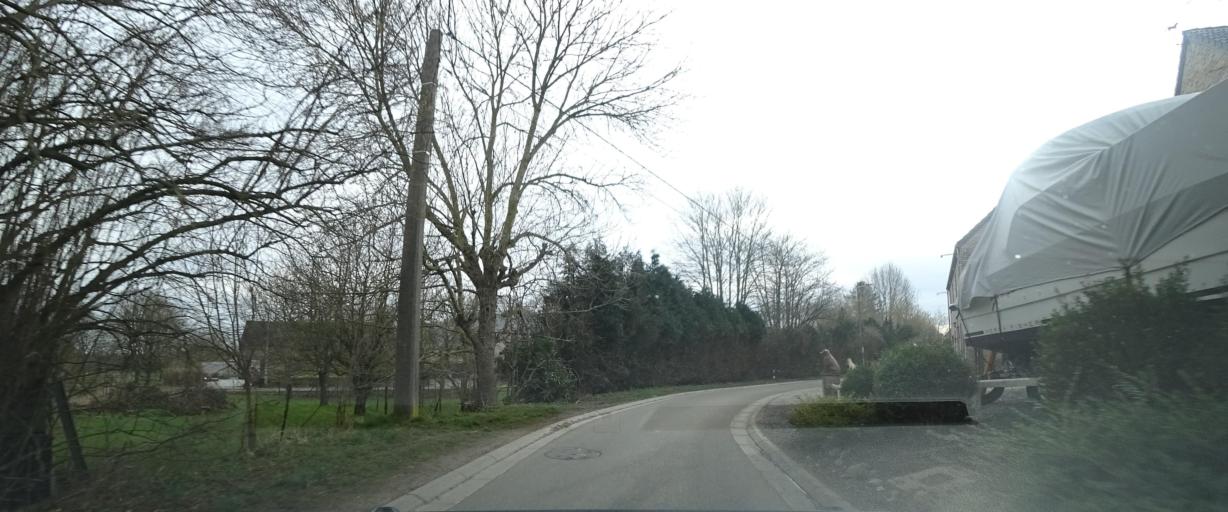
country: BE
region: Wallonia
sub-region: Province de Namur
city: Sombreffe
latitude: 50.4972
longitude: 4.6333
